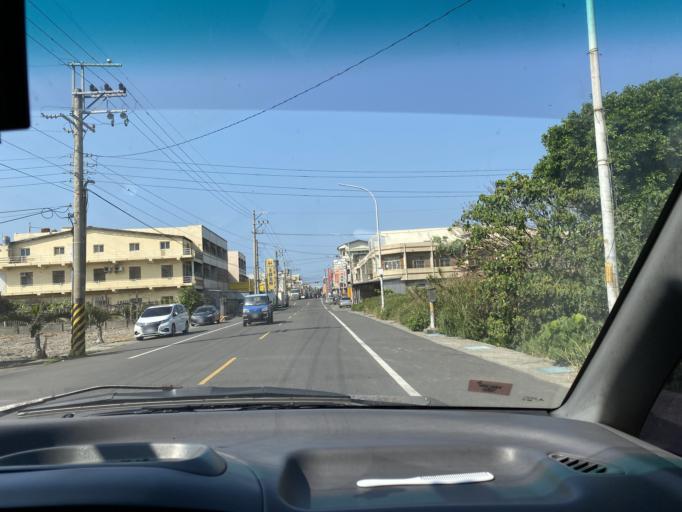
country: TW
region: Taiwan
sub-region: Changhua
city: Chang-hua
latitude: 23.9594
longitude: 120.3368
